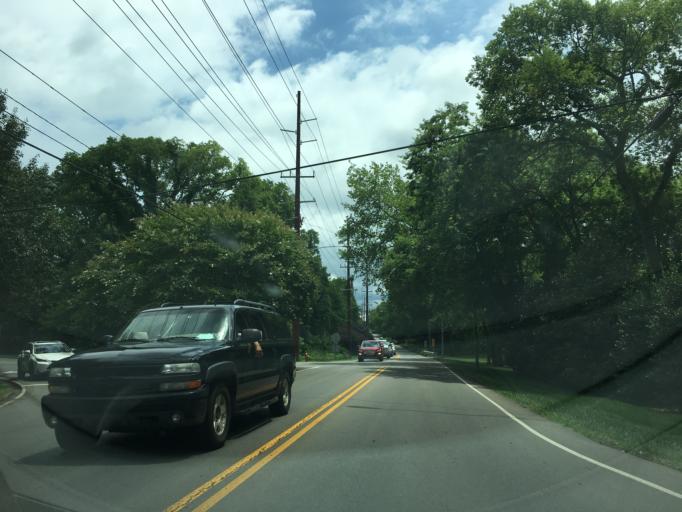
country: US
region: Tennessee
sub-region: Davidson County
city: Belle Meade
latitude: 36.0930
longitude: -86.8491
